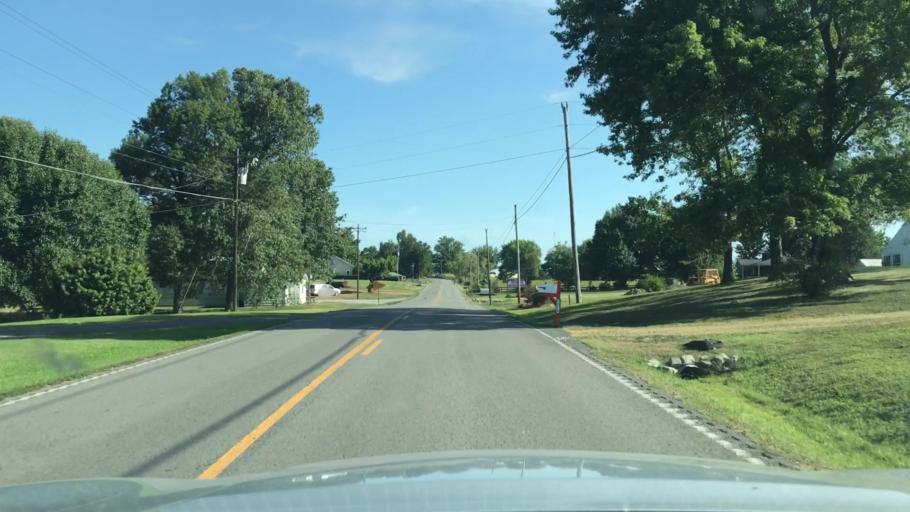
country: US
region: Kentucky
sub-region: Muhlenberg County
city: Greenville
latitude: 37.1563
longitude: -87.1419
